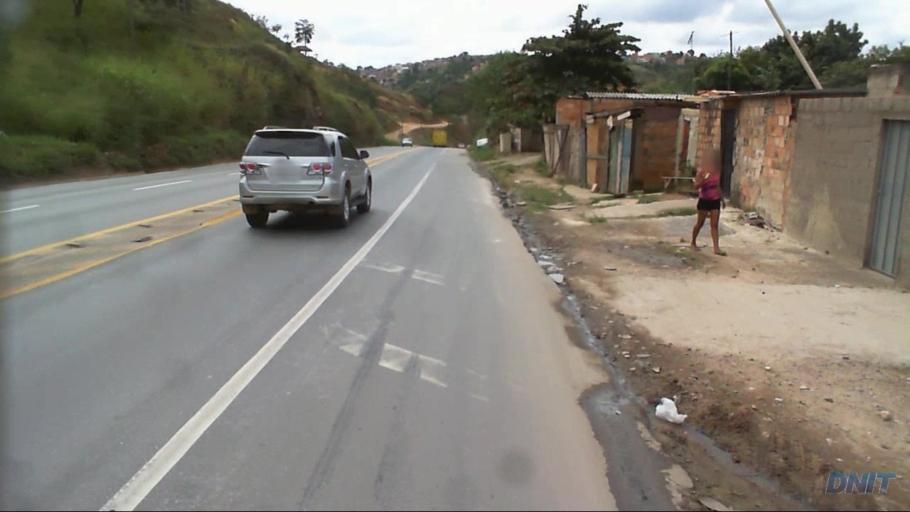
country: BR
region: Minas Gerais
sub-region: Santa Luzia
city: Santa Luzia
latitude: -19.8413
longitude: -43.8853
